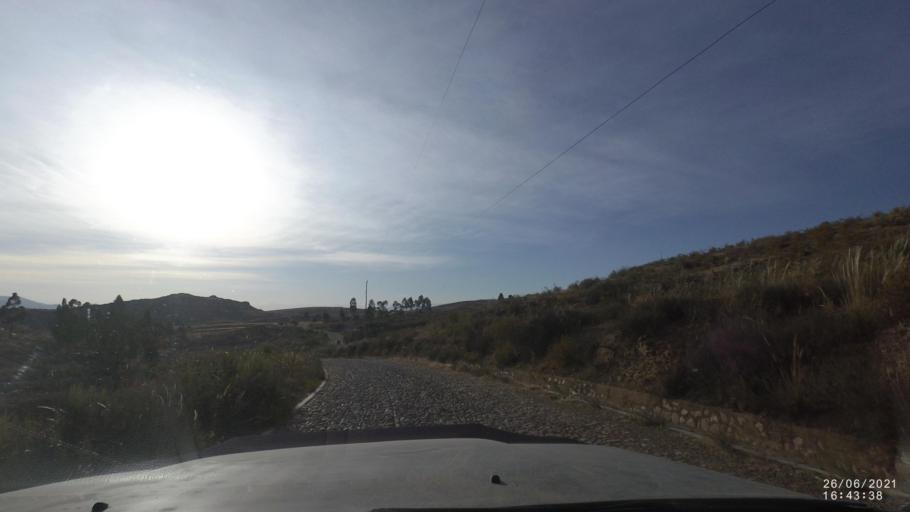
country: BO
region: Cochabamba
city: Cliza
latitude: -17.7571
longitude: -65.8330
